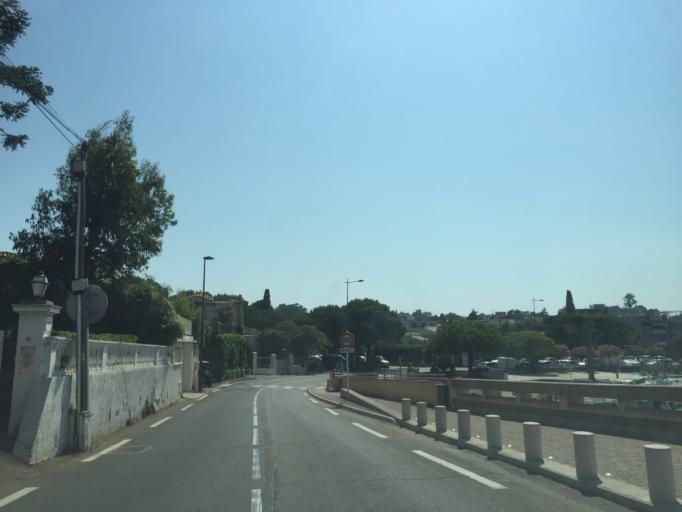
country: FR
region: Provence-Alpes-Cote d'Azur
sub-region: Departement des Alpes-Maritimes
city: Antibes
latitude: 43.5693
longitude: 7.1321
